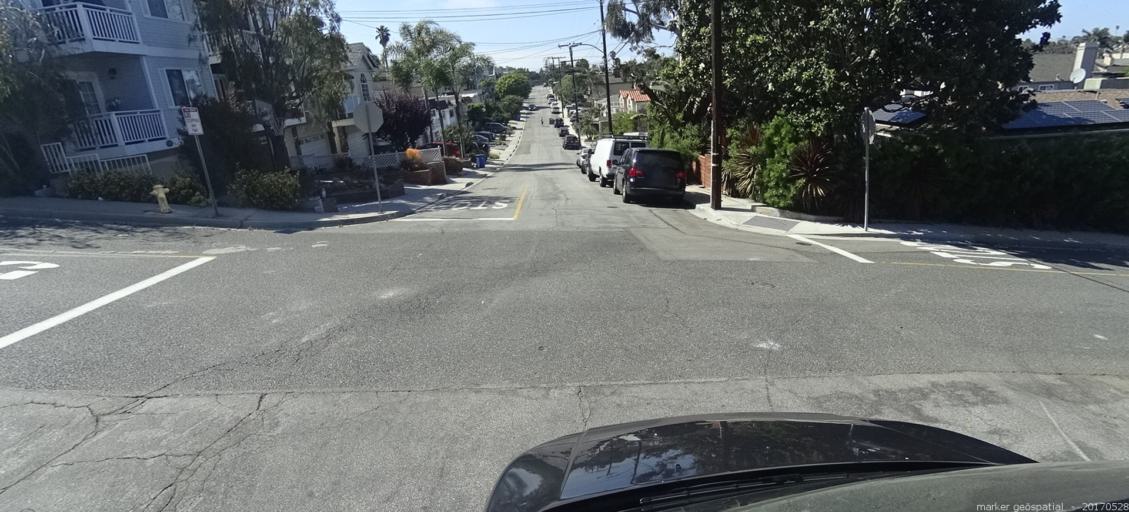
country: US
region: California
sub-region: Los Angeles County
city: Hermosa Beach
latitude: 33.8699
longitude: -118.3887
